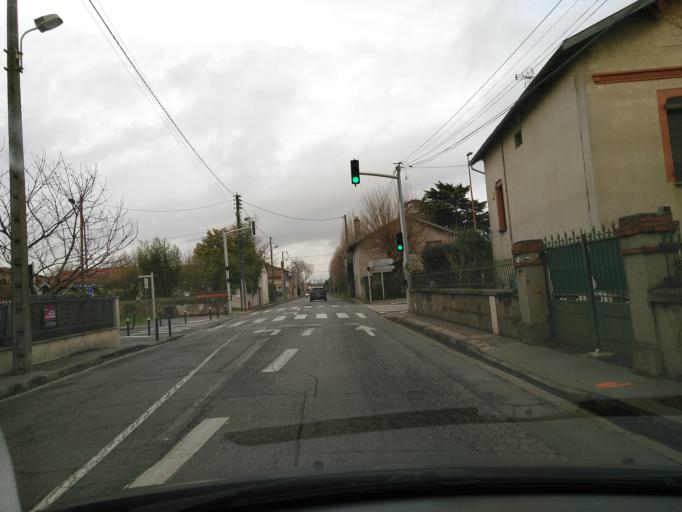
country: FR
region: Midi-Pyrenees
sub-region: Departement de la Haute-Garonne
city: Toulouse
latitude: 43.6309
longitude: 1.4381
